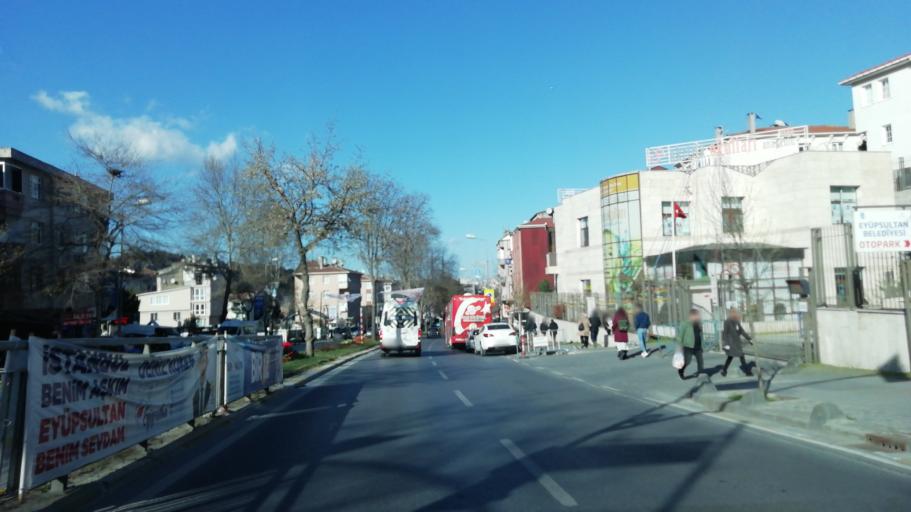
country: TR
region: Istanbul
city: Istanbul
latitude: 41.0438
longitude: 28.9295
